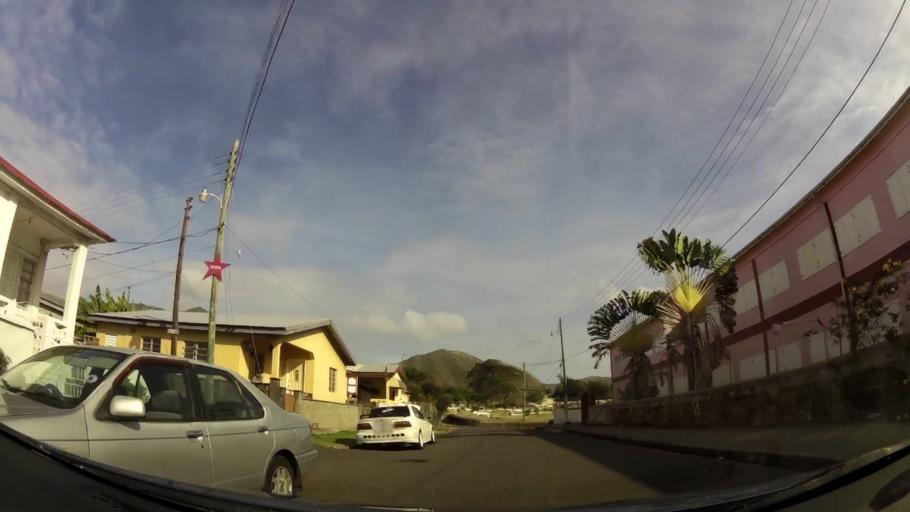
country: KN
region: Saint George Basseterre
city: Basseterre
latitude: 17.2960
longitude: -62.7334
